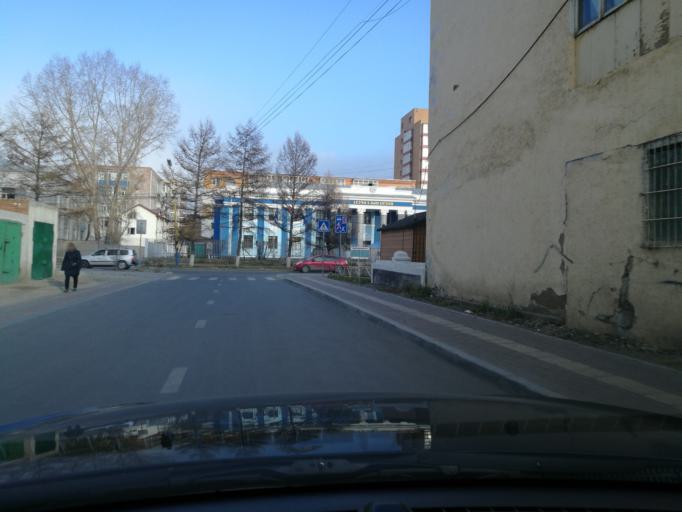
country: MN
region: Ulaanbaatar
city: Ulaanbaatar
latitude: 47.9247
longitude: 106.9269
